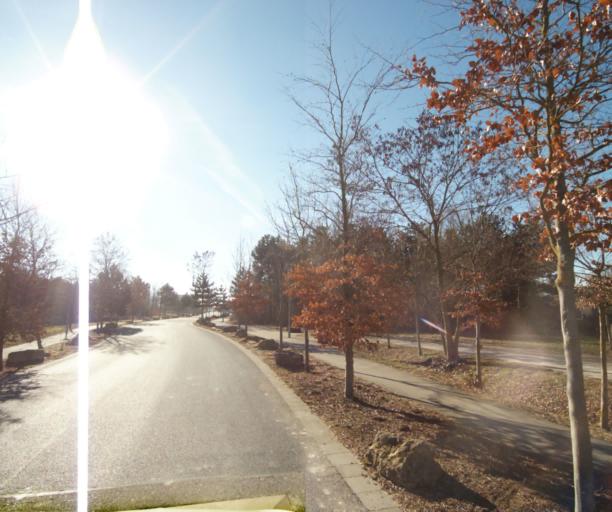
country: FR
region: Lorraine
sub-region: Departement de Meurthe-et-Moselle
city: Maxeville
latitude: 48.7057
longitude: 6.1493
